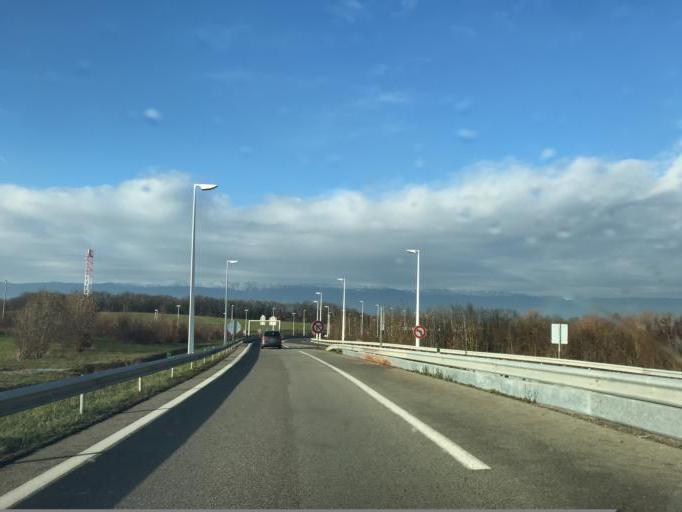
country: FR
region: Rhone-Alpes
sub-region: Departement de la Haute-Savoie
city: Neydens
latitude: 46.1345
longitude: 6.1027
